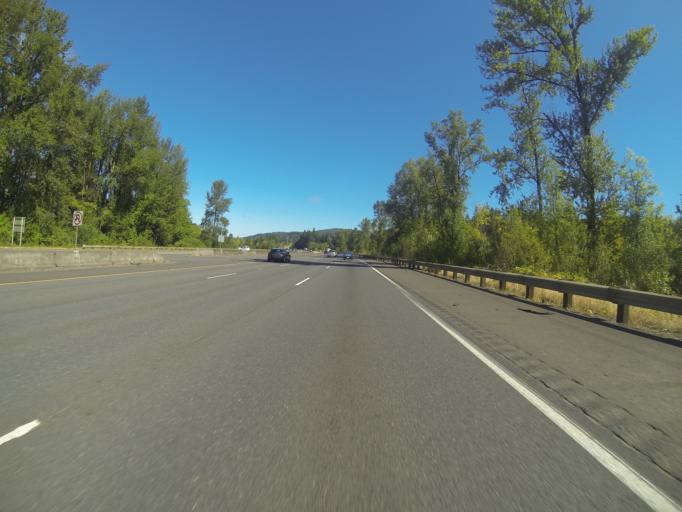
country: US
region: Oregon
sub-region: Columbia County
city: Rainier
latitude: 46.0765
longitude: -122.8666
